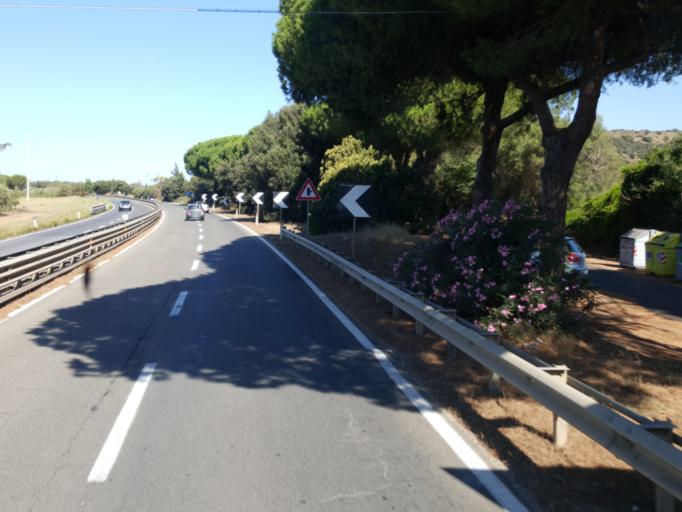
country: IT
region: Tuscany
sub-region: Provincia di Grosseto
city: Orbetello Scalo
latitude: 42.4364
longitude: 11.2793
